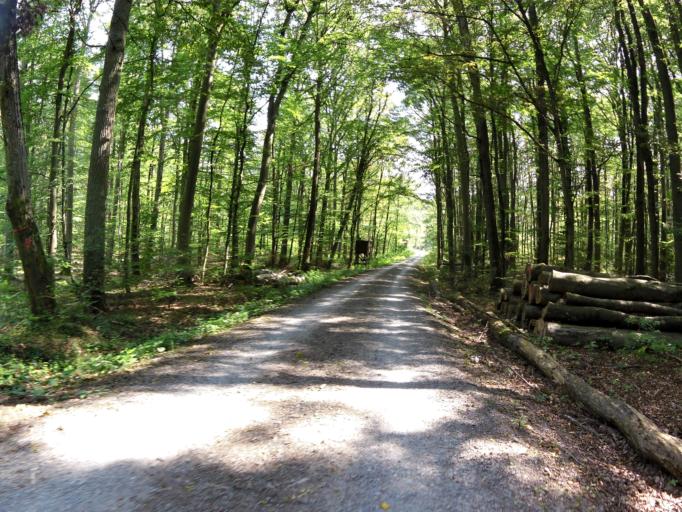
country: DE
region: Bavaria
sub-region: Regierungsbezirk Unterfranken
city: Waldbrunn
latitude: 49.7167
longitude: 9.8041
